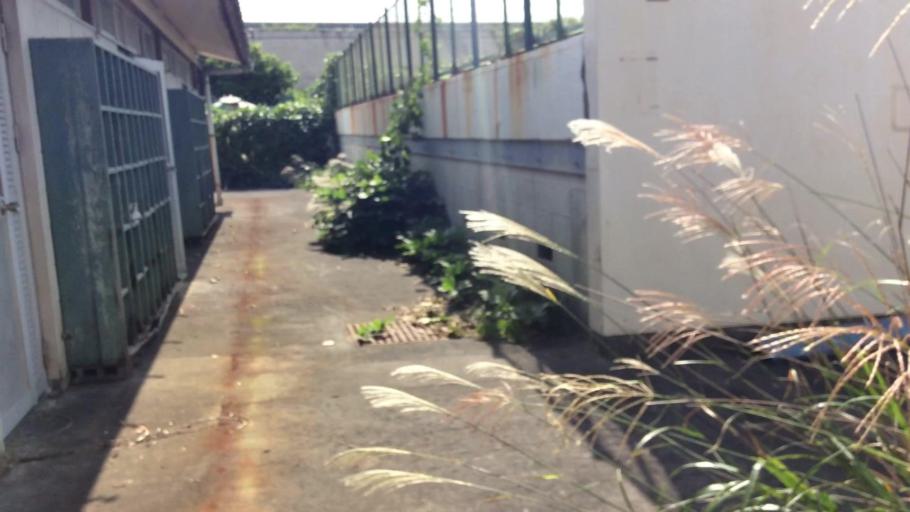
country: JP
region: Shizuoka
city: Fuji
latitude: 35.1173
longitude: 138.6270
